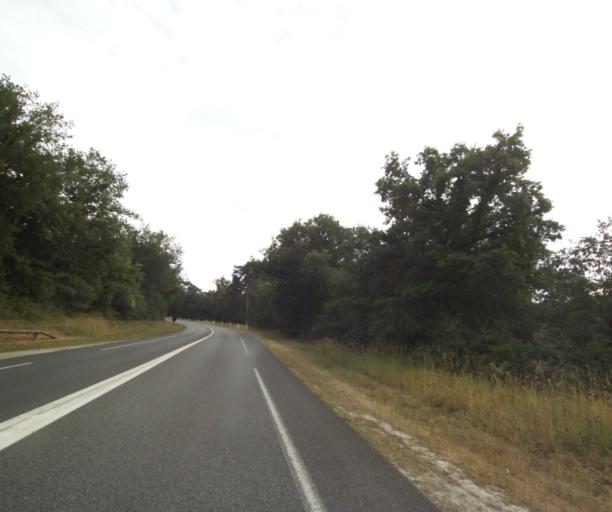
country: FR
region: Ile-de-France
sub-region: Departement de Seine-et-Marne
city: Bois-le-Roi
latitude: 48.4393
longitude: 2.6904
